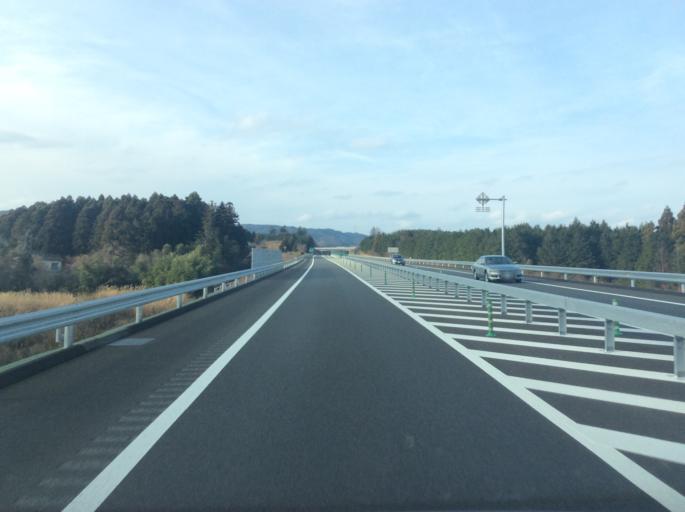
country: JP
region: Fukushima
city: Namie
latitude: 37.4873
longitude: 140.9511
